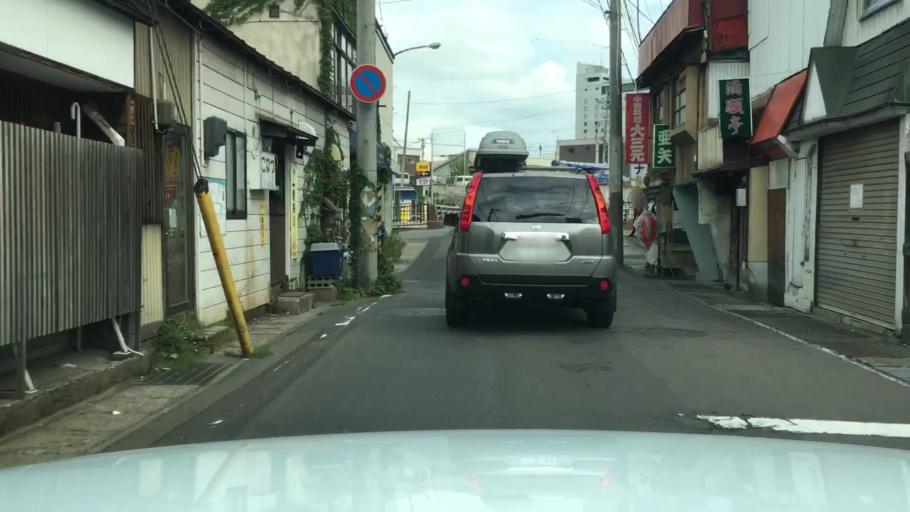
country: JP
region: Aomori
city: Hirosaki
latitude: 40.6001
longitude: 140.4720
